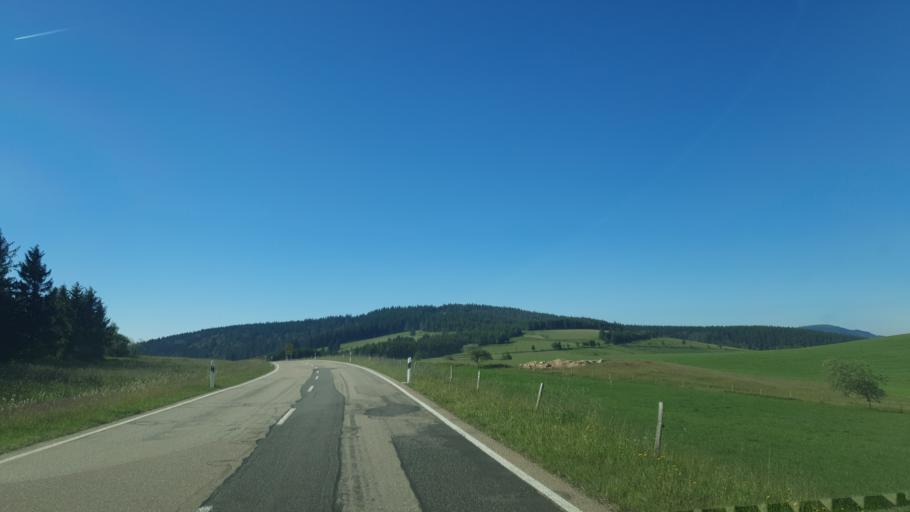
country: DE
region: Baden-Wuerttemberg
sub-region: Freiburg Region
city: Horben
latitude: 47.8961
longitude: 7.8903
